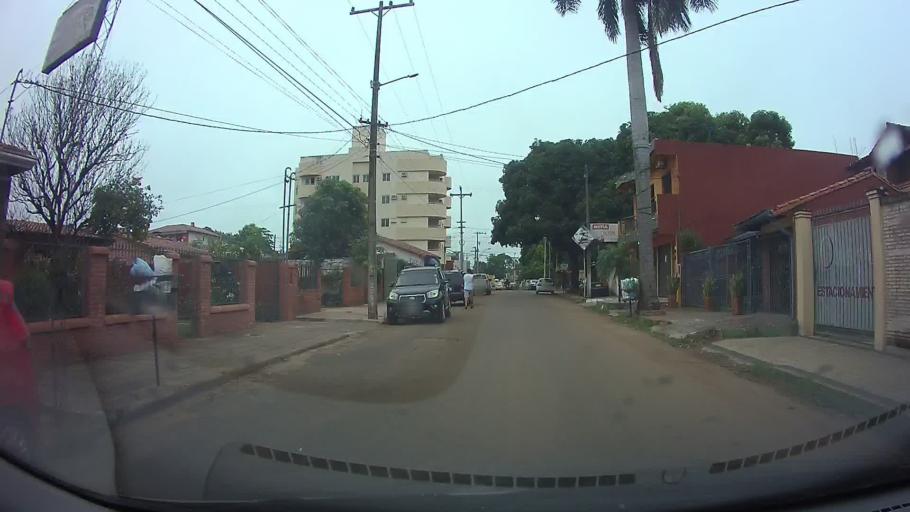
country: PY
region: Central
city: Itaugua
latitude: -25.3917
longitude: -57.3531
